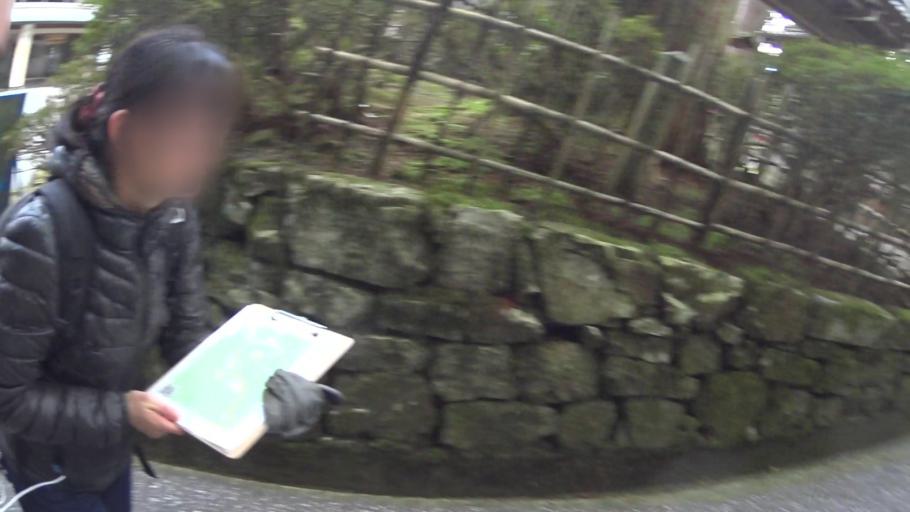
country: JP
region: Shiga Prefecture
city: Otsu-shi
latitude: 35.0681
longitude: 135.8417
